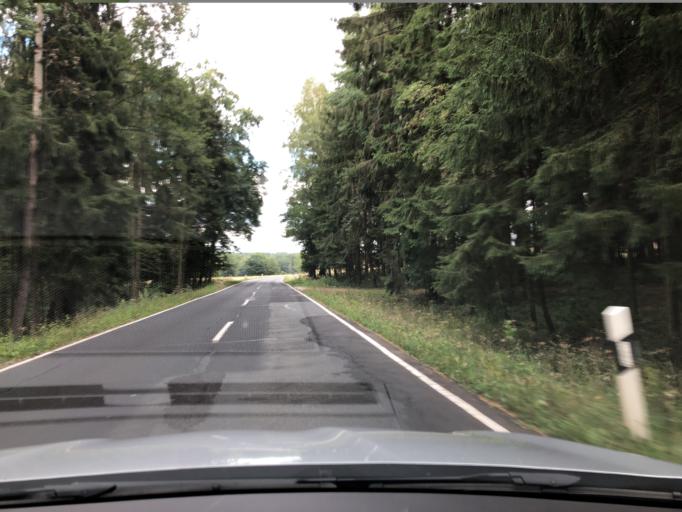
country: DE
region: Bavaria
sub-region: Upper Palatinate
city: Poppenricht
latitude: 49.4898
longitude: 11.8063
